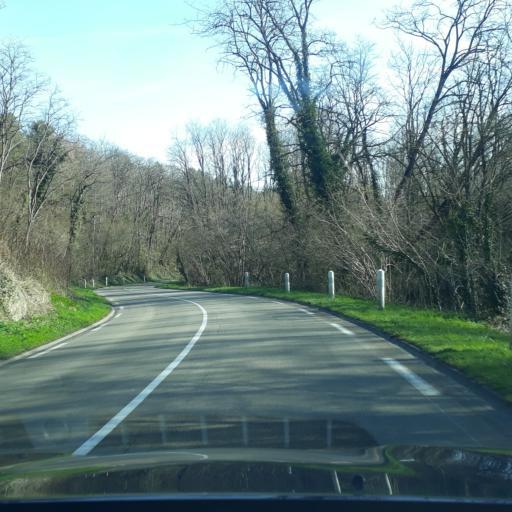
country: FR
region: Ile-de-France
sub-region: Departement de l'Essonne
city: Boissy-le-Cutte
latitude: 48.4621
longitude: 2.2684
